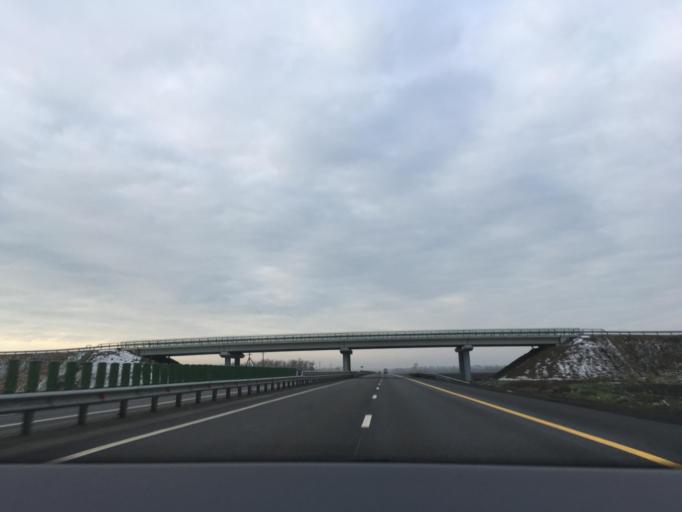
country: RU
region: Krasnodarskiy
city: Lenina
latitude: 46.0979
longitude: 39.8080
